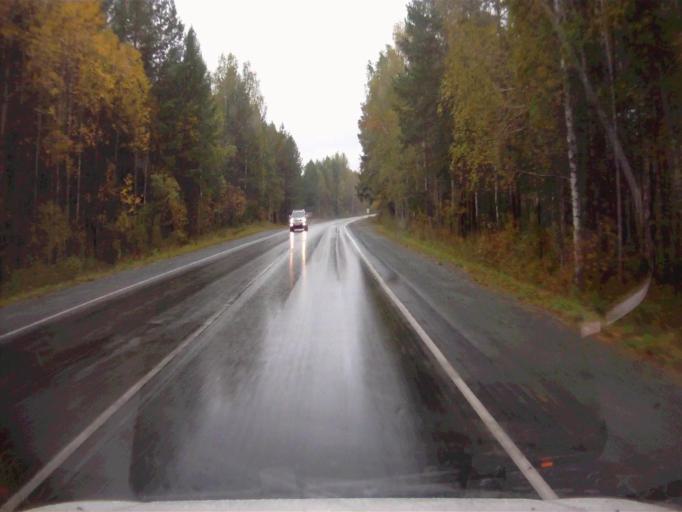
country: RU
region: Chelyabinsk
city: Tayginka
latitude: 55.5950
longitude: 60.6209
